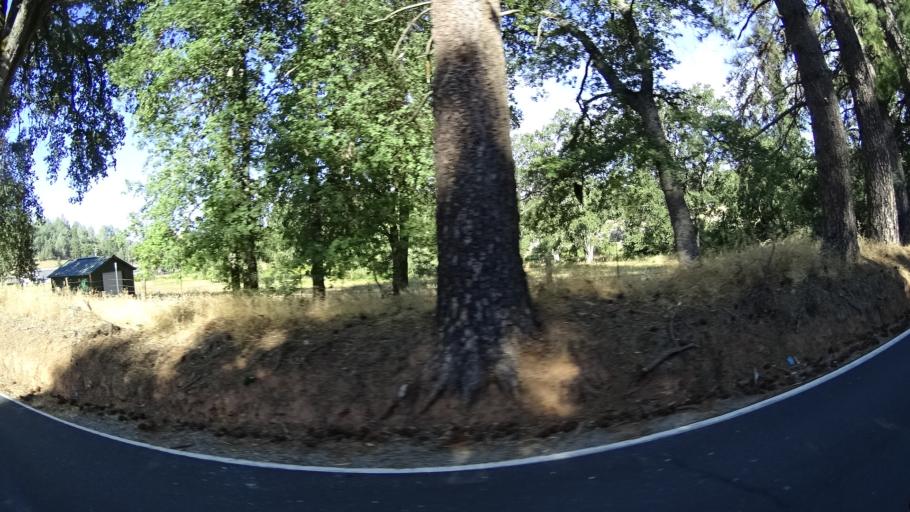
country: US
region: California
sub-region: Amador County
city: Pioneer
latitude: 38.3821
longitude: -120.5327
